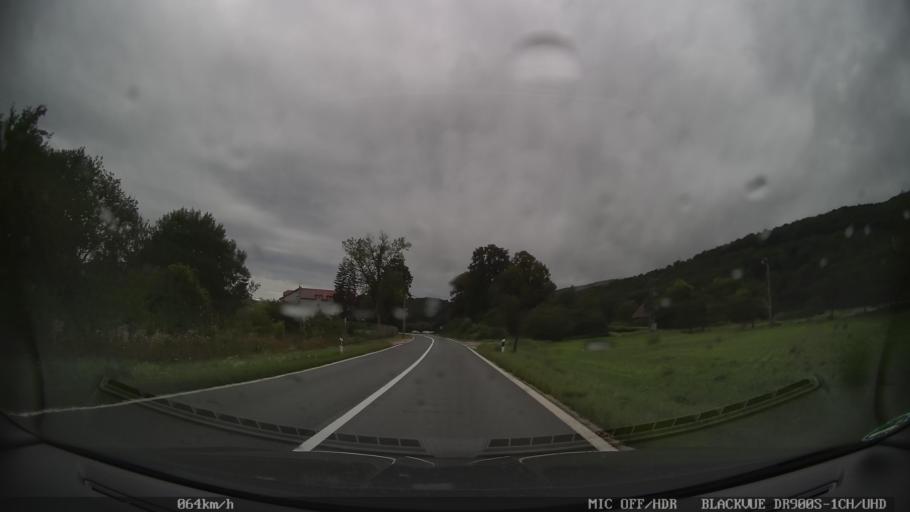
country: HR
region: Licko-Senjska
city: Brinje
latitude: 44.9401
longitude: 15.1259
